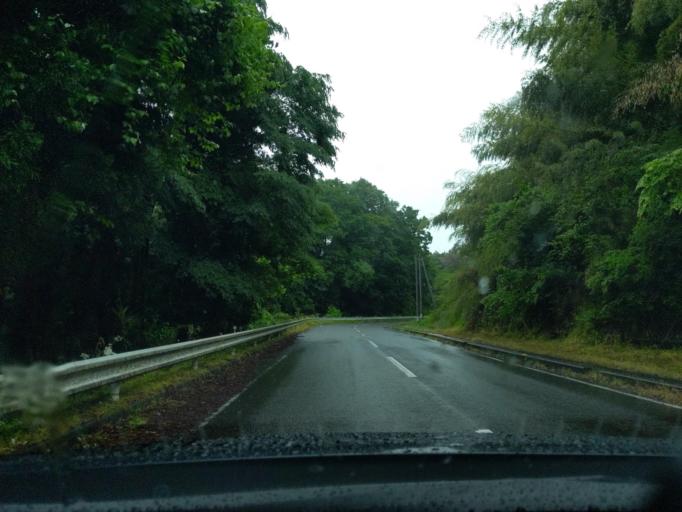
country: JP
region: Fukushima
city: Nihommatsu
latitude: 37.5611
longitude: 140.5357
